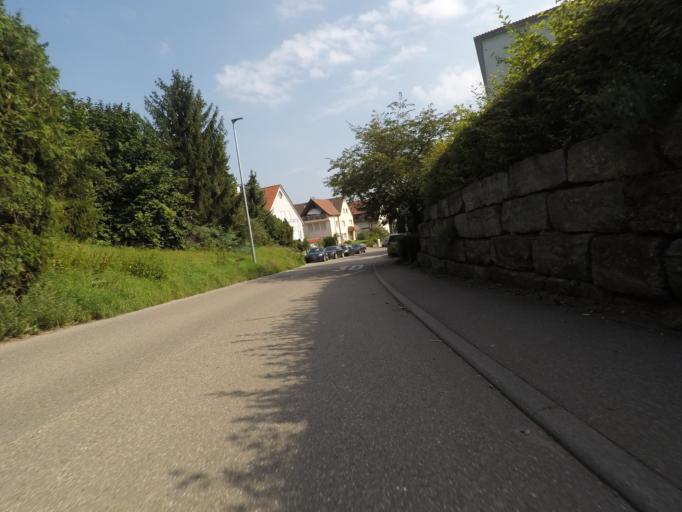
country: DE
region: Baden-Wuerttemberg
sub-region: Regierungsbezirk Stuttgart
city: Weinstadt-Endersbach
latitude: 48.8039
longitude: 9.3817
